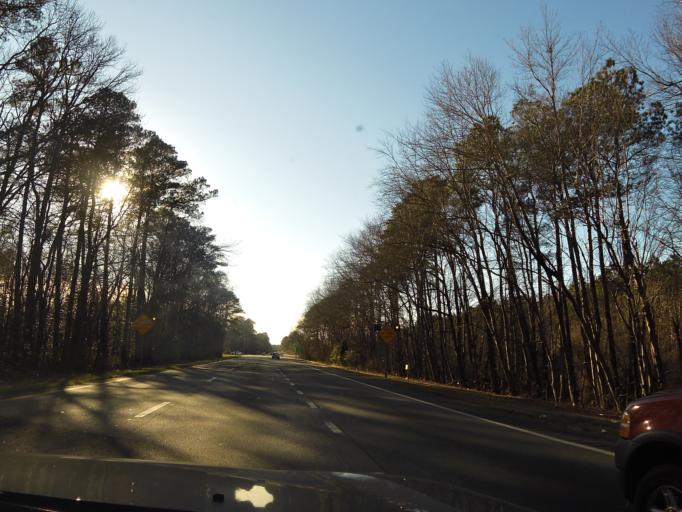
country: US
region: Virginia
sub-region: City of Suffolk
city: Suffolk
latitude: 36.7574
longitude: -76.5064
